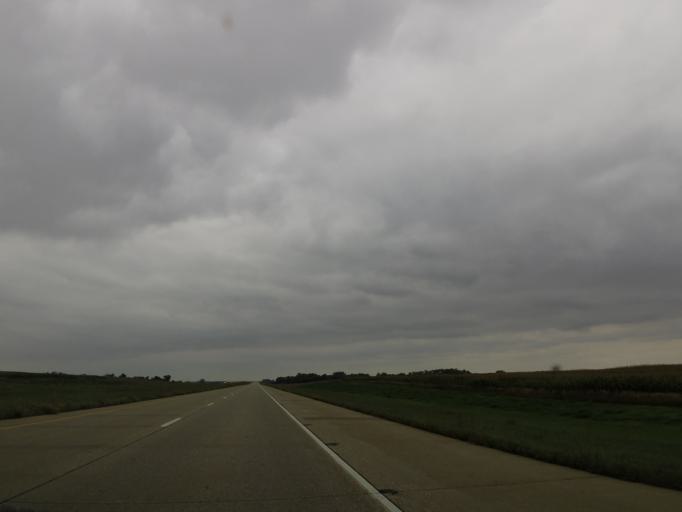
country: US
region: South Dakota
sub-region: Roberts County
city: Sisseton
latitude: 45.5778
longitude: -96.9892
